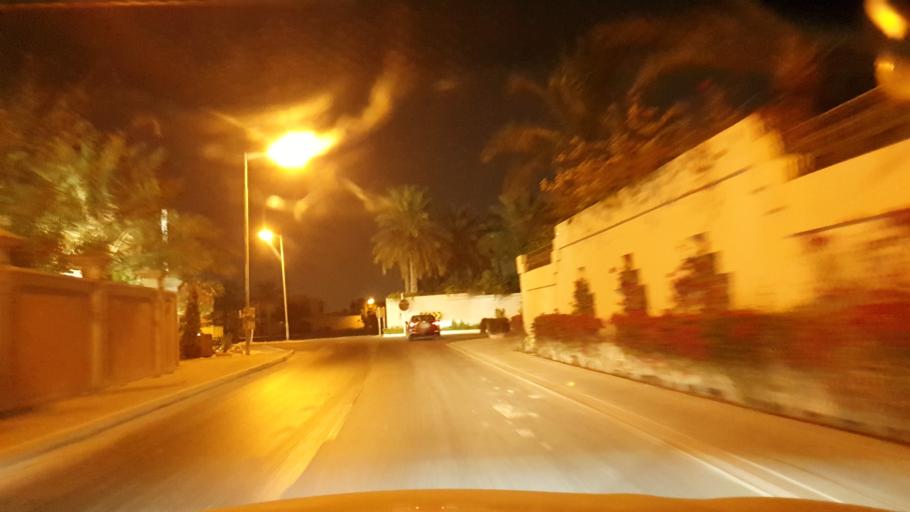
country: BH
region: Manama
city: Jidd Hafs
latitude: 26.1975
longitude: 50.4944
